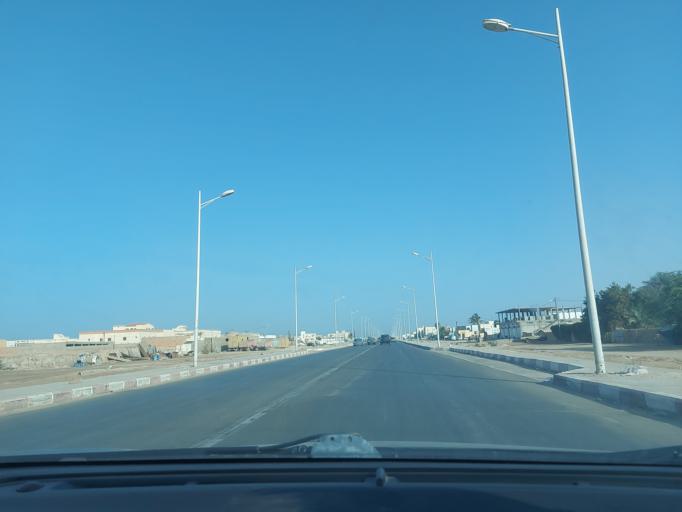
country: MR
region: Nouakchott
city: Nouakchott
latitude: 18.0914
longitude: -16.0101
